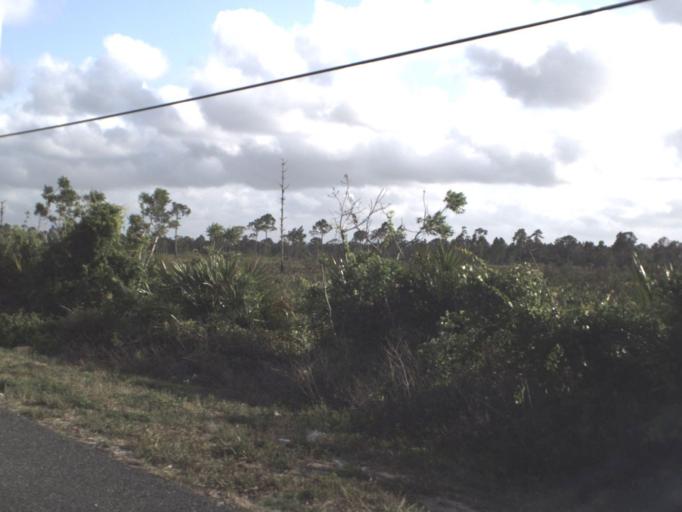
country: US
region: Florida
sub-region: Brevard County
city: Mims
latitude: 28.7534
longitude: -80.8737
